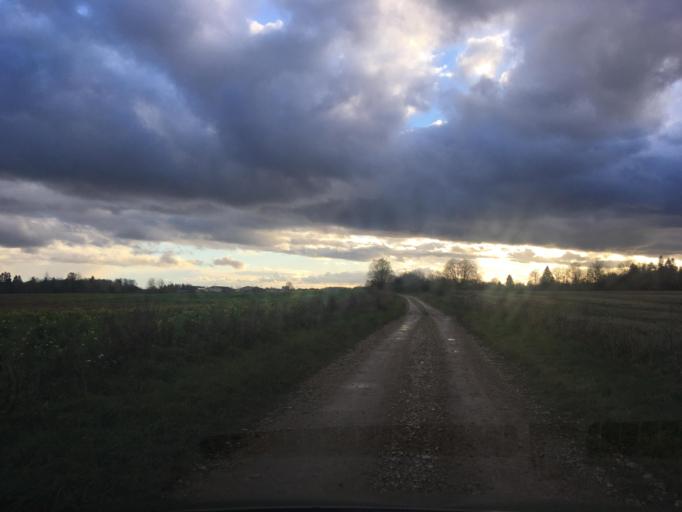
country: EE
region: Harju
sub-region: Raasiku vald
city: Arukula
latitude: 59.3536
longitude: 25.1092
